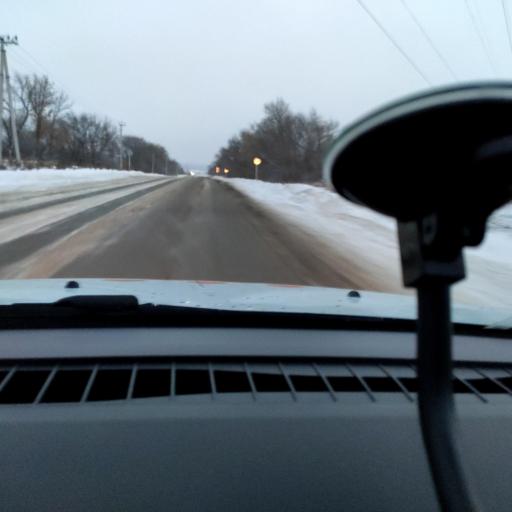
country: RU
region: Samara
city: Kurumoch
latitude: 53.4786
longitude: 50.0273
